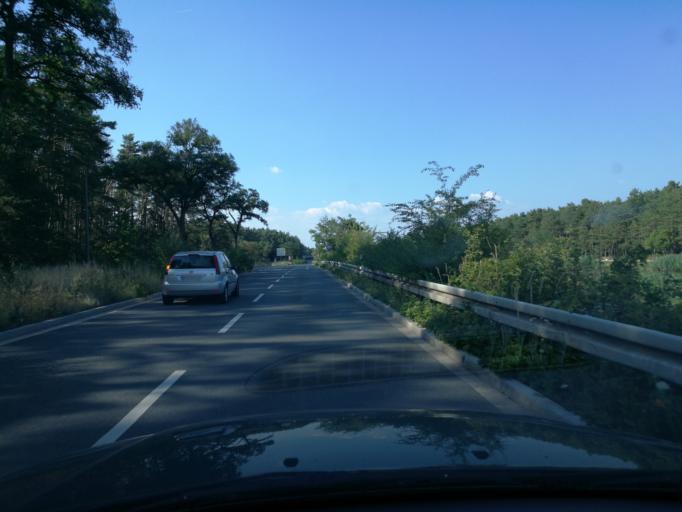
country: DE
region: Bavaria
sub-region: Regierungsbezirk Mittelfranken
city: Erlangen
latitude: 49.6042
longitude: 10.9717
